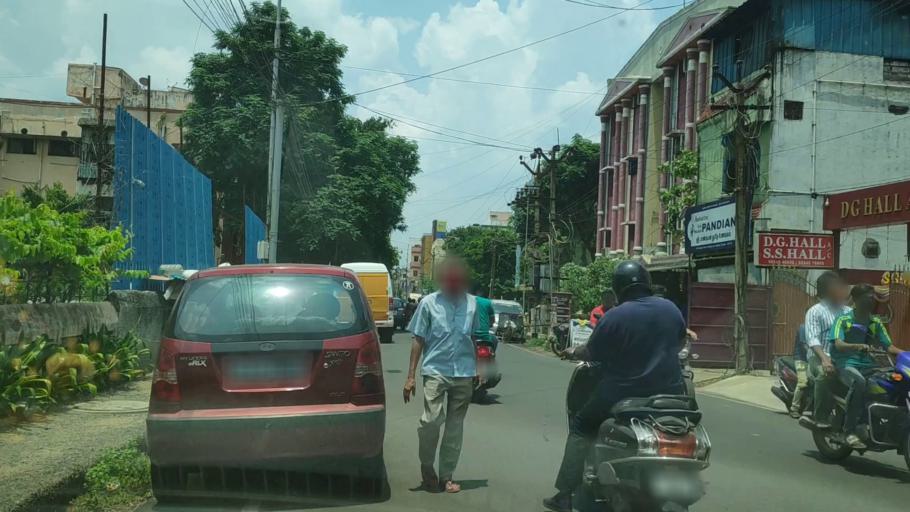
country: IN
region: Tamil Nadu
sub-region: Thiruvallur
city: Ambattur
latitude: 13.1199
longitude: 80.1512
